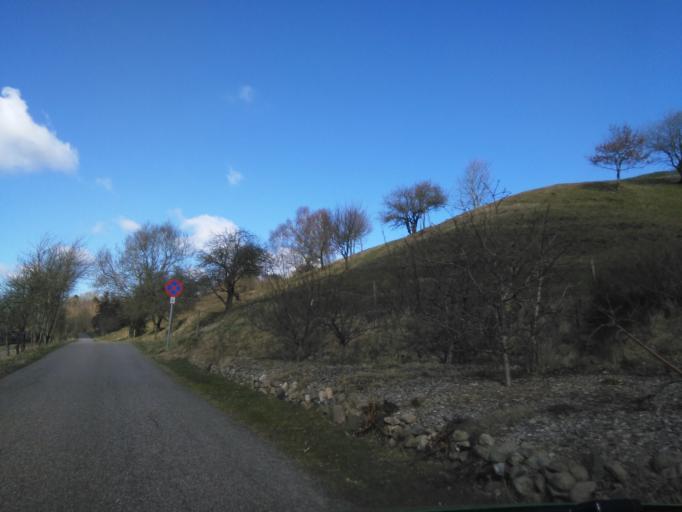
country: DK
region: Central Jutland
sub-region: Skanderborg Kommune
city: Ry
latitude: 56.1079
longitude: 9.7377
